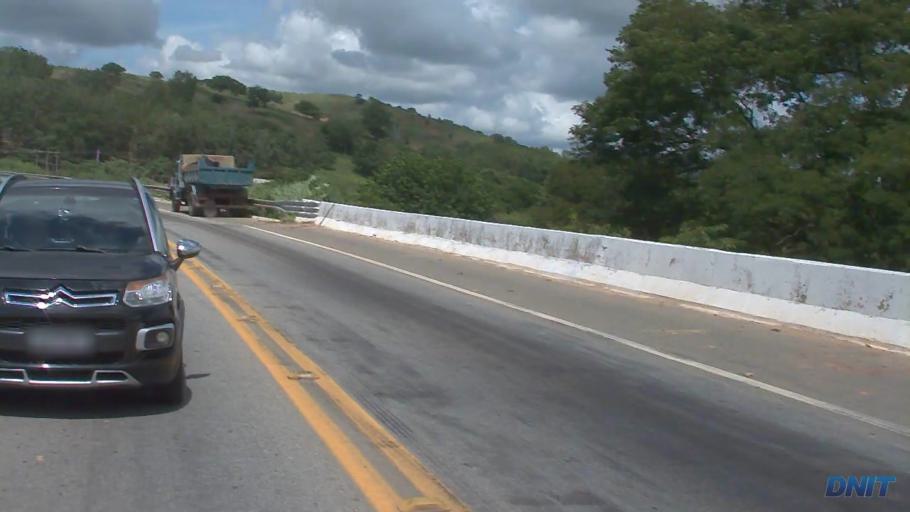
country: BR
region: Minas Gerais
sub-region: Governador Valadares
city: Governador Valadares
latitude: -18.8977
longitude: -42.0042
